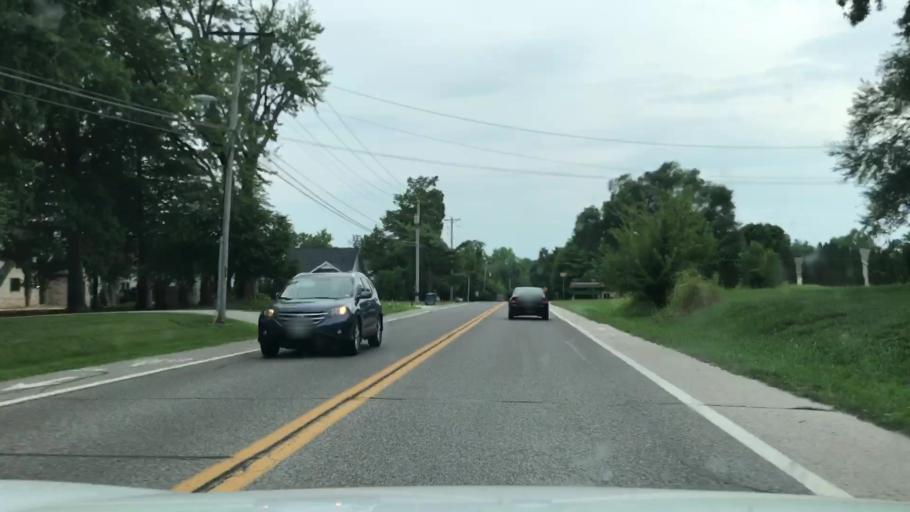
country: US
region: Missouri
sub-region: Saint Louis County
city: Chesterfield
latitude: 38.6563
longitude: -90.5876
